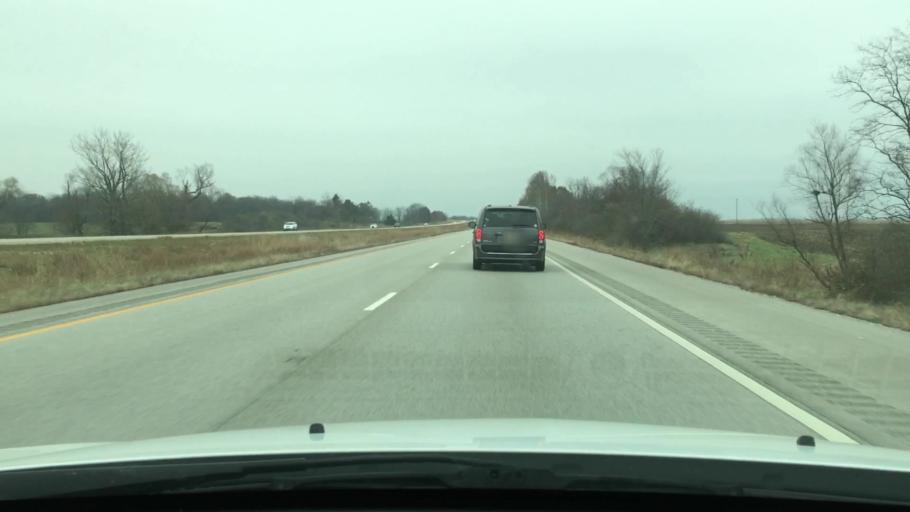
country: US
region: Illinois
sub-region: Sangamon County
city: New Berlin
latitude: 39.7398
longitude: -89.9651
